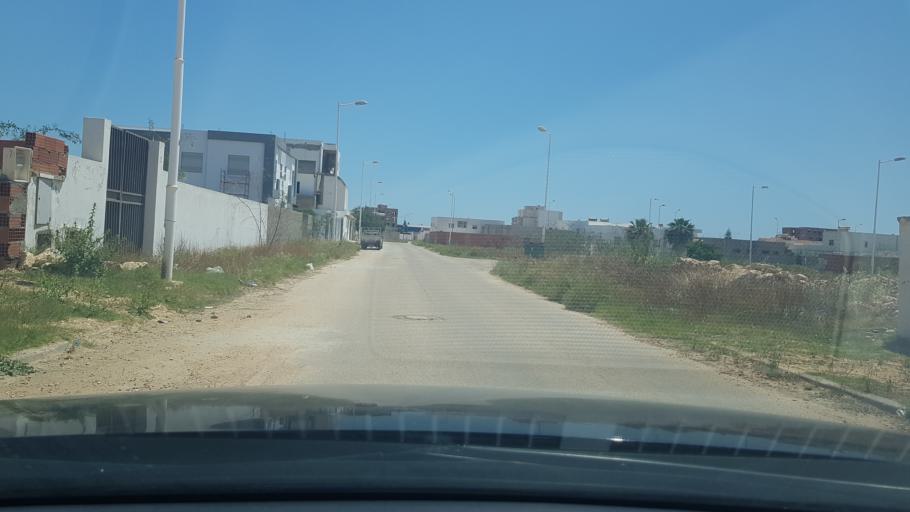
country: TN
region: Safaqis
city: Al Qarmadah
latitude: 34.8390
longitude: 10.7610
